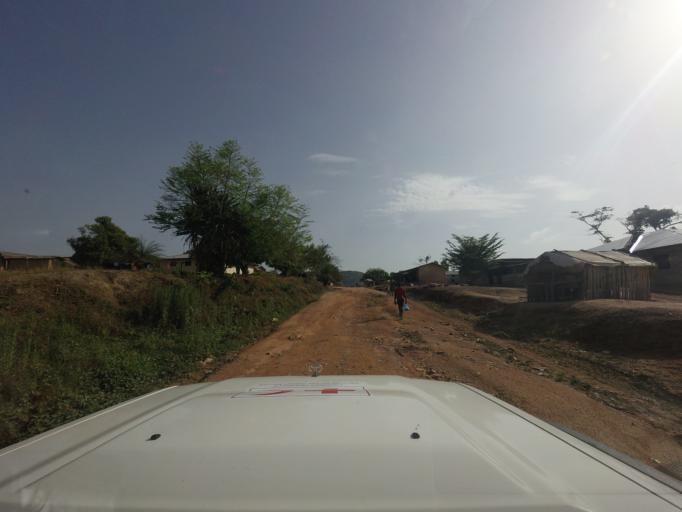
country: LR
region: Lofa
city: Voinjama
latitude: 8.4303
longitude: -9.7478
